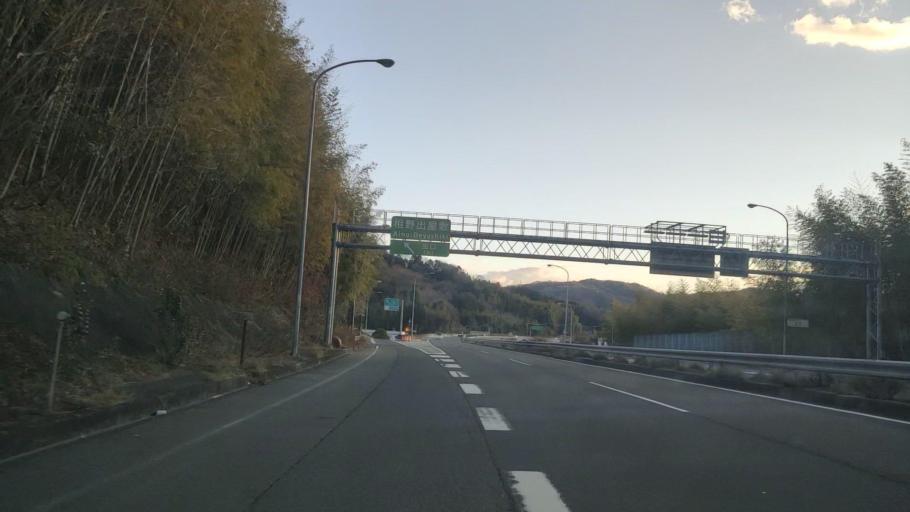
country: JP
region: Hyogo
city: Tatsunocho-tominaga
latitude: 34.8659
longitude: 134.6184
